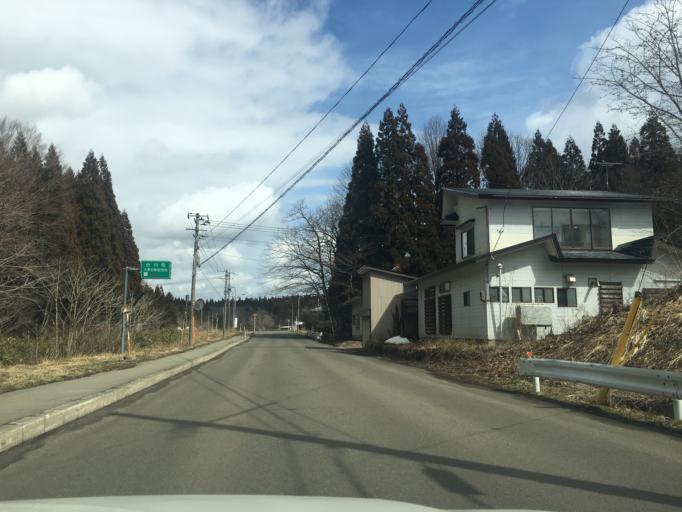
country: JP
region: Akita
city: Takanosu
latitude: 40.1869
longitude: 140.3410
